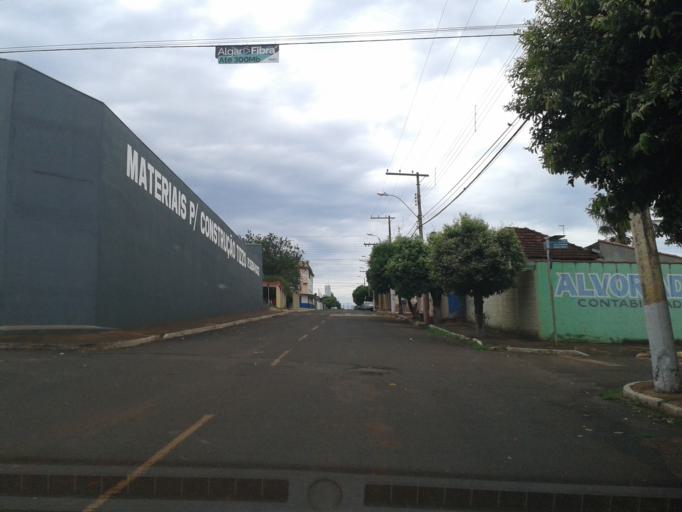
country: BR
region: Goias
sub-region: Itumbiara
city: Itumbiara
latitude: -18.4369
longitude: -49.1869
